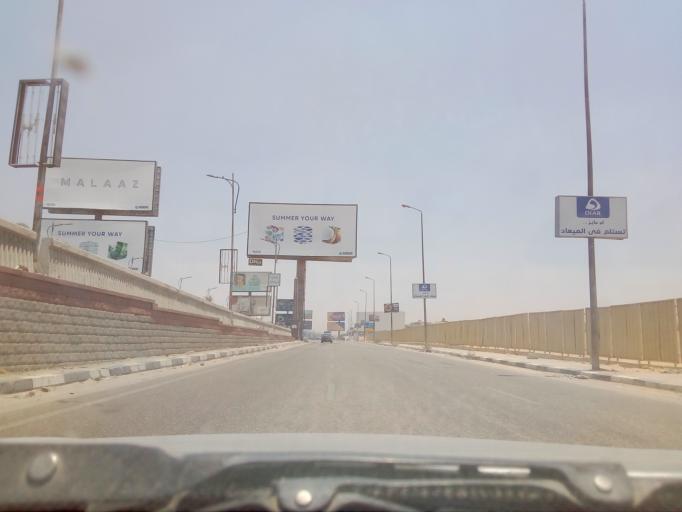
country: EG
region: Muhafazat al Qahirah
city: Cairo
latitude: 30.0159
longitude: 31.4037
